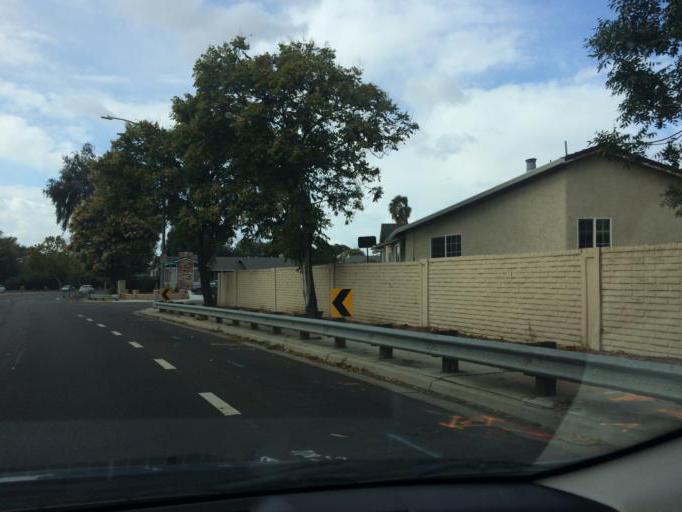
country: US
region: California
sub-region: Santa Clara County
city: Seven Trees
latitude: 37.2979
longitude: -121.7960
